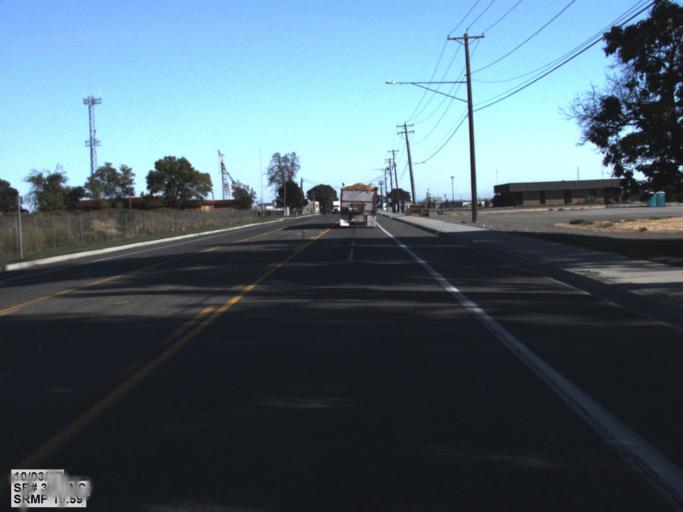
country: US
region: Washington
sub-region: Franklin County
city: Pasco
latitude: 46.2200
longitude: -119.0856
